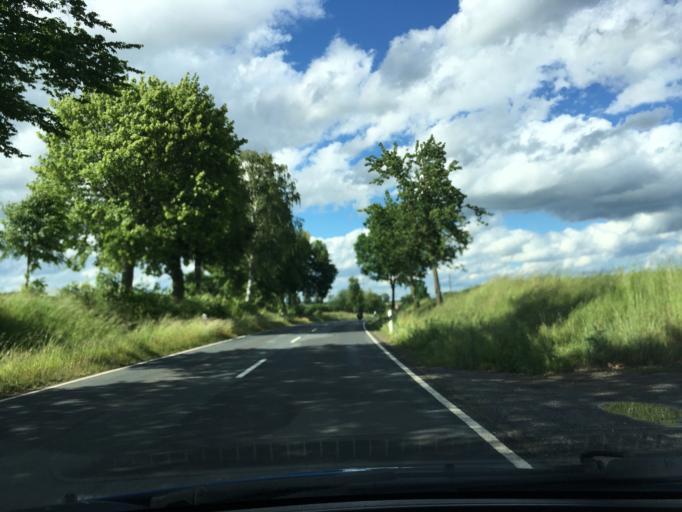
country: DE
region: Lower Saxony
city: Hardegsen
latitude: 51.6246
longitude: 9.8511
